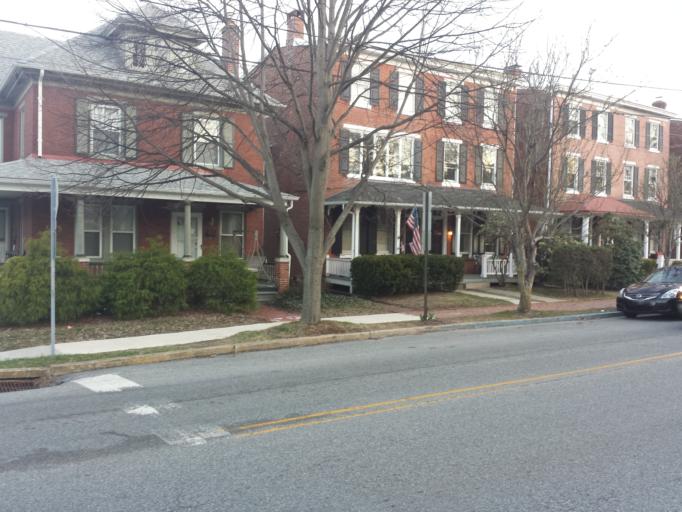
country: US
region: Pennsylvania
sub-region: Chester County
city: West Chester
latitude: 39.9550
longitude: -75.6021
